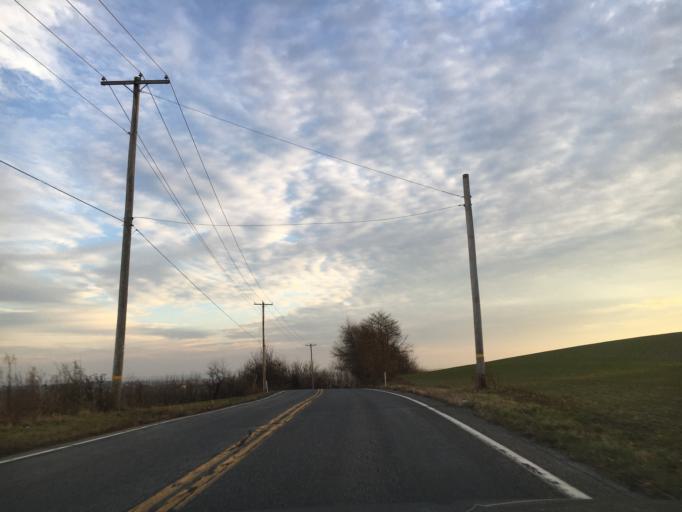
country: US
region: Pennsylvania
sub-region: Lehigh County
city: Slatington
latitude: 40.7118
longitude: -75.5966
